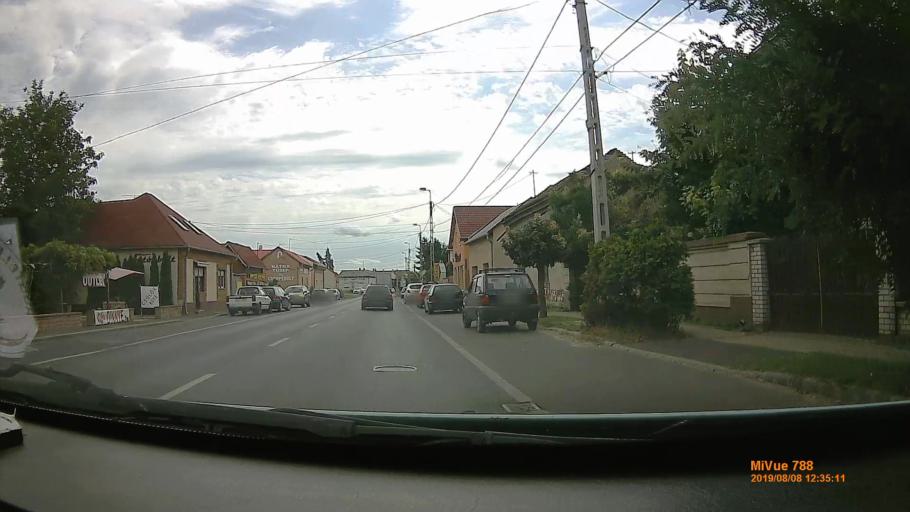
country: HU
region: Szabolcs-Szatmar-Bereg
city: Nyirbator
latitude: 47.8361
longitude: 22.1258
